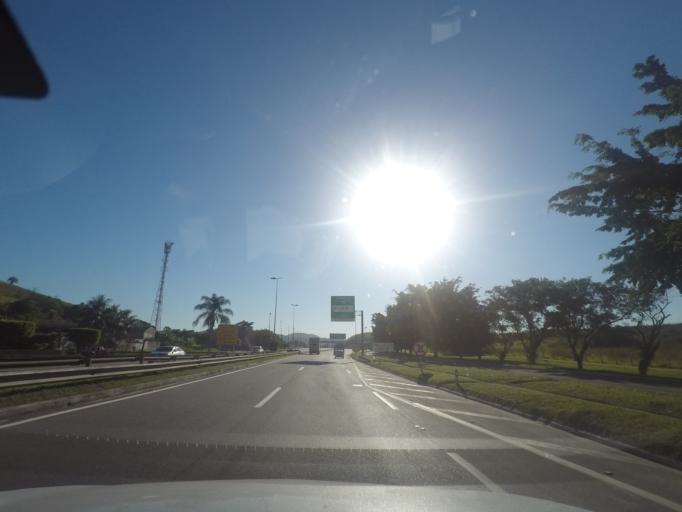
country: BR
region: Rio de Janeiro
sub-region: Petropolis
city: Petropolis
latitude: -22.6469
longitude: -43.1919
